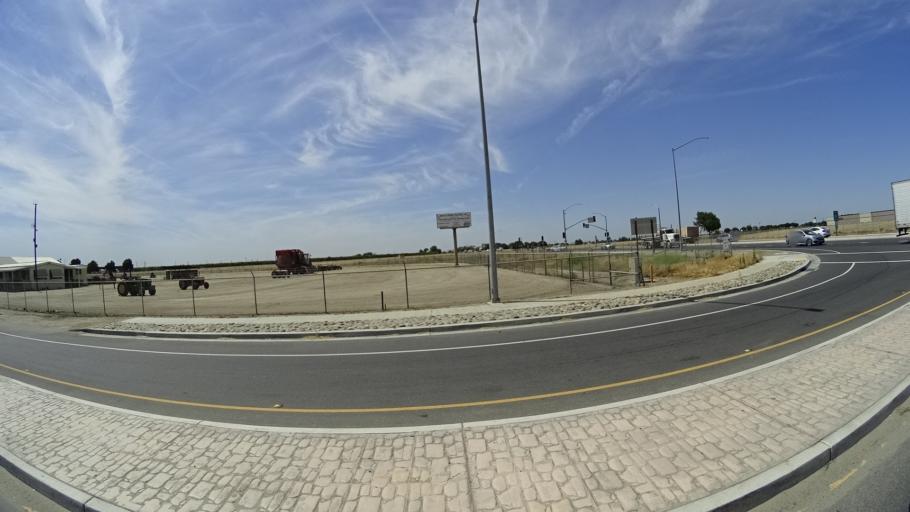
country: US
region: California
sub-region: Kings County
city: Home Garden
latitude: 36.3280
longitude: -119.6007
